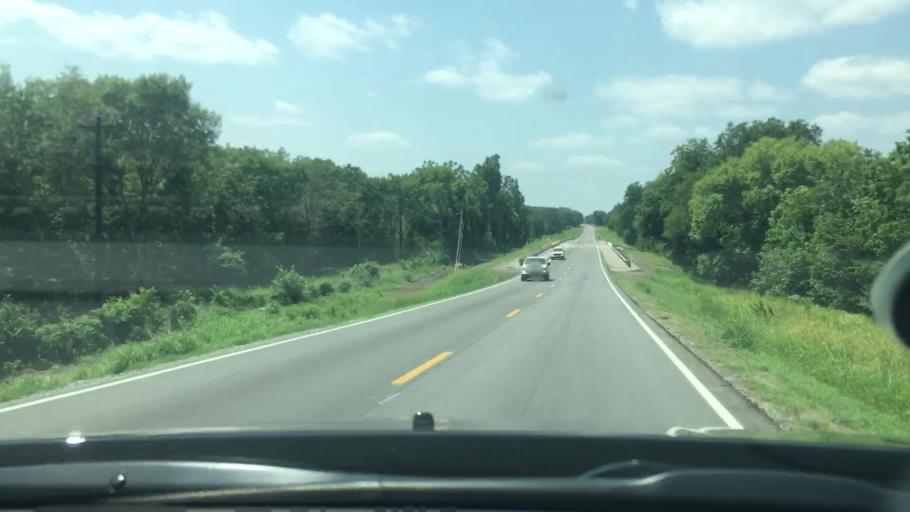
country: US
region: Oklahoma
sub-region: Atoka County
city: Atoka
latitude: 34.3791
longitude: -96.2768
